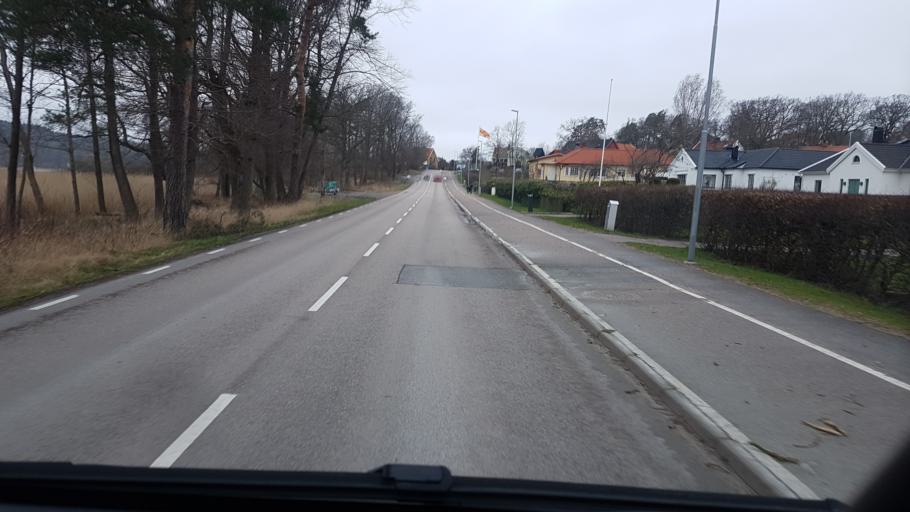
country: SE
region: Vaestra Goetaland
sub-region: Lerums Kommun
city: Lerum
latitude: 57.7700
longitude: 12.2500
